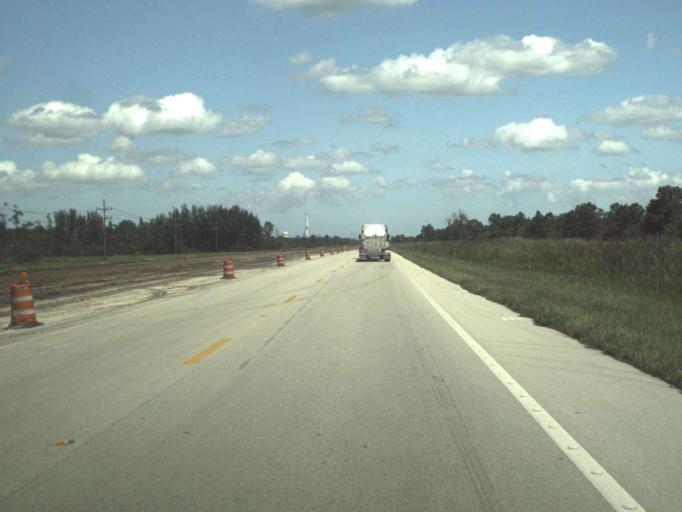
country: US
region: Florida
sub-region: Martin County
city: Indiantown
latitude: 26.9288
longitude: -80.3306
